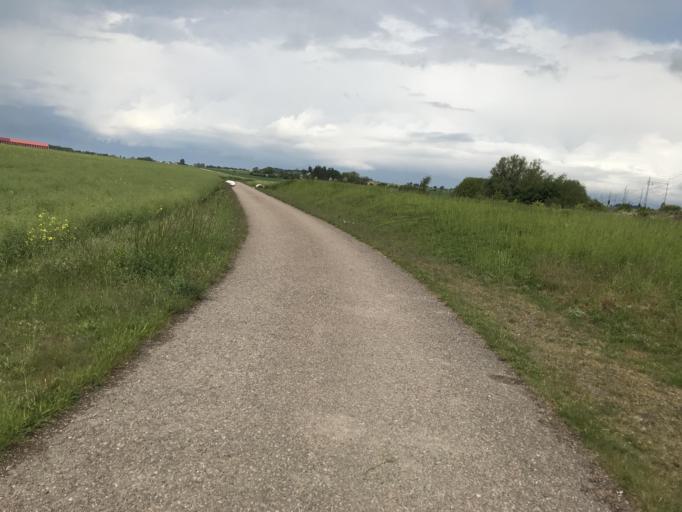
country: SE
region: Skane
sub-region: Landskrona
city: Landskrona
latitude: 55.9025
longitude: 12.8482
